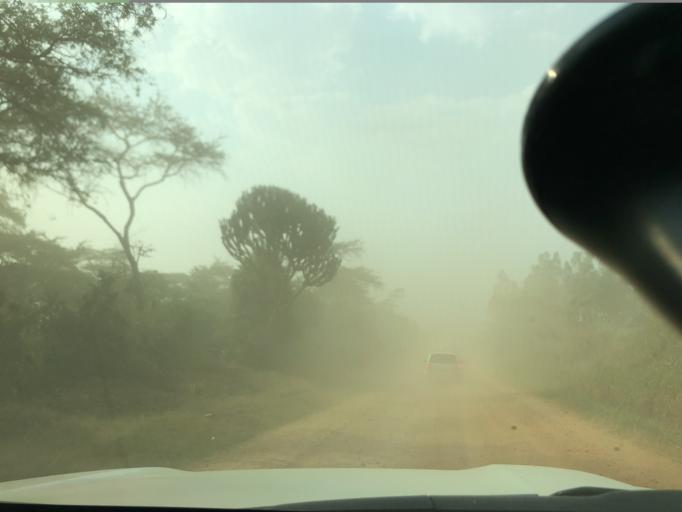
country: CD
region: Nord Kivu
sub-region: North Kivu
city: Butembo
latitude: 0.0673
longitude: 29.6596
